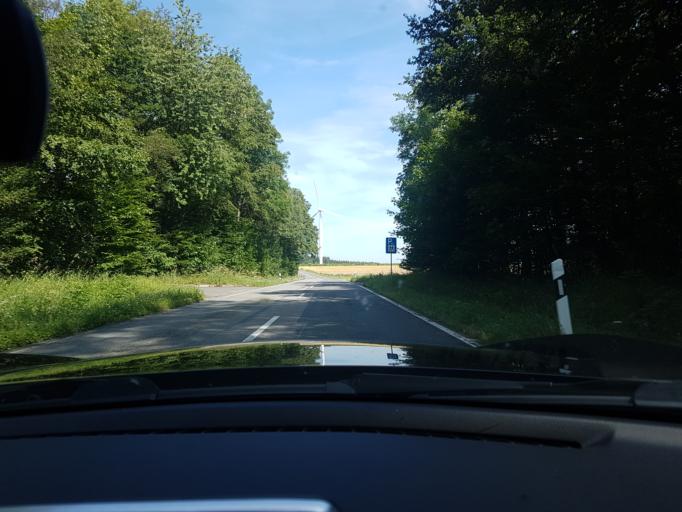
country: DE
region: Baden-Wuerttemberg
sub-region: Karlsruhe Region
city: Seckach
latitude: 49.4492
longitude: 9.2735
